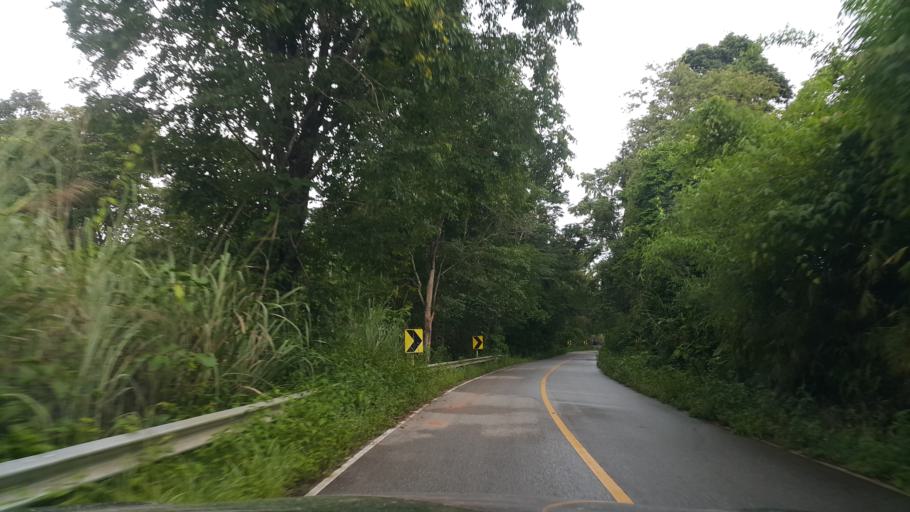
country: TH
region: Loei
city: Na Haeo
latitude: 17.4870
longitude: 100.8054
